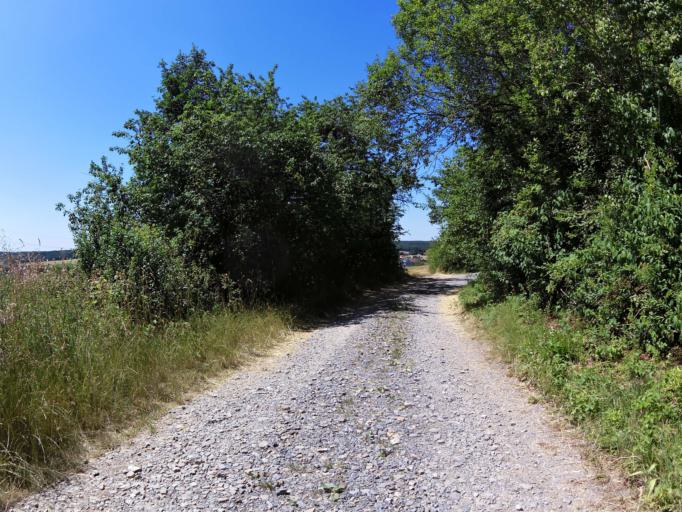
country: DE
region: Bavaria
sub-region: Regierungsbezirk Unterfranken
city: Kleinrinderfeld
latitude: 49.7008
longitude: 9.8563
